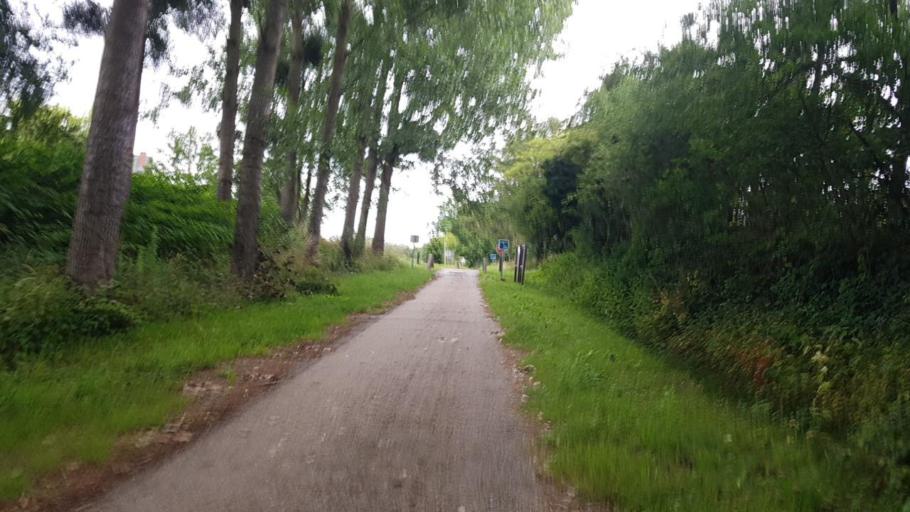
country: FR
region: Picardie
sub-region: Departement de l'Aisne
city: Buironfosse
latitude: 49.9024
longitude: 3.8190
